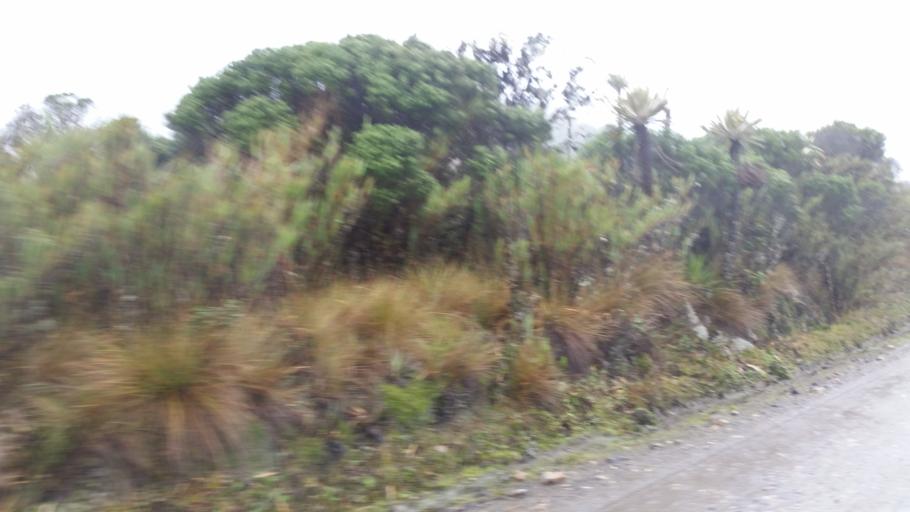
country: CO
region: Cundinamarca
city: La Calera
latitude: 4.6980
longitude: -73.8024
